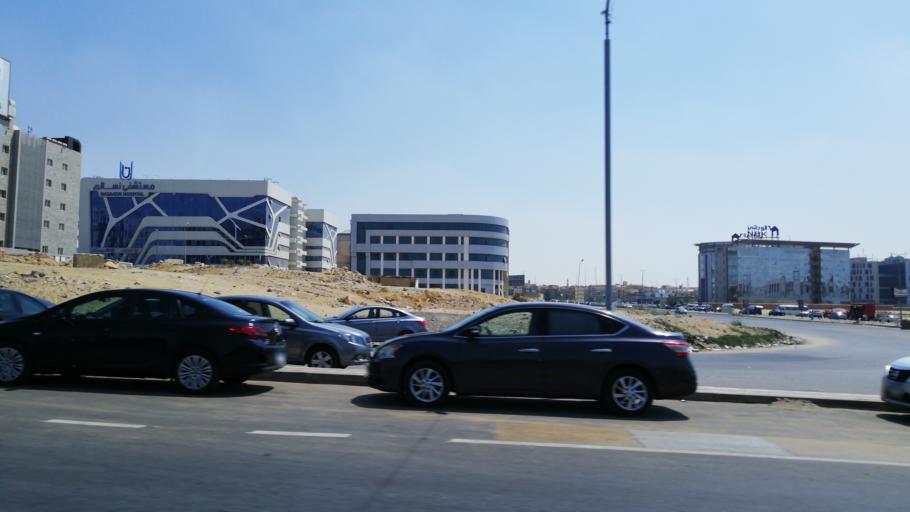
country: EG
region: Muhafazat al Qahirah
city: Cairo
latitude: 30.0213
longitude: 31.4332
